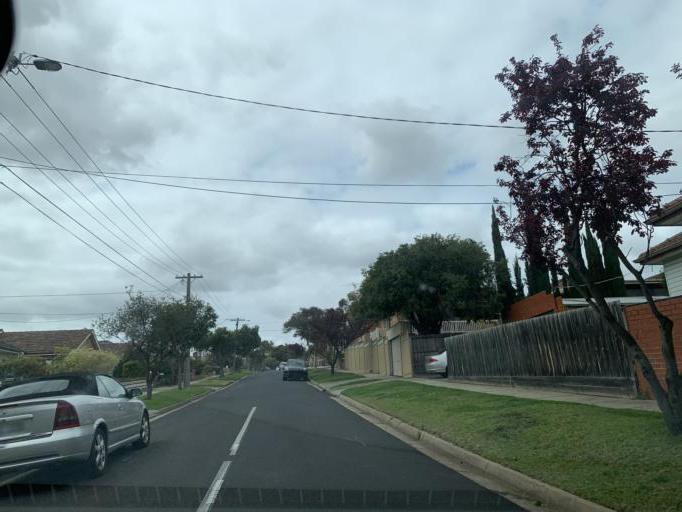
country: AU
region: Victoria
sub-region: Moreland
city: Pascoe Vale South
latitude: -37.7468
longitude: 144.9391
